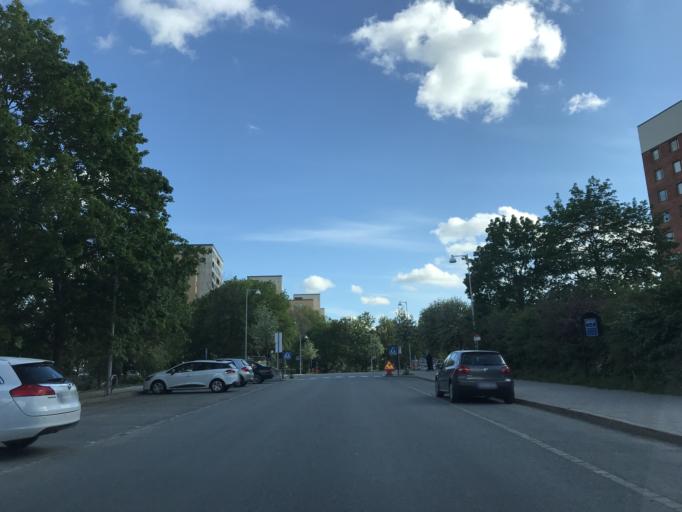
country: SE
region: Stockholm
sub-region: Solna Kommun
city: Solna
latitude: 59.3498
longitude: 17.9964
